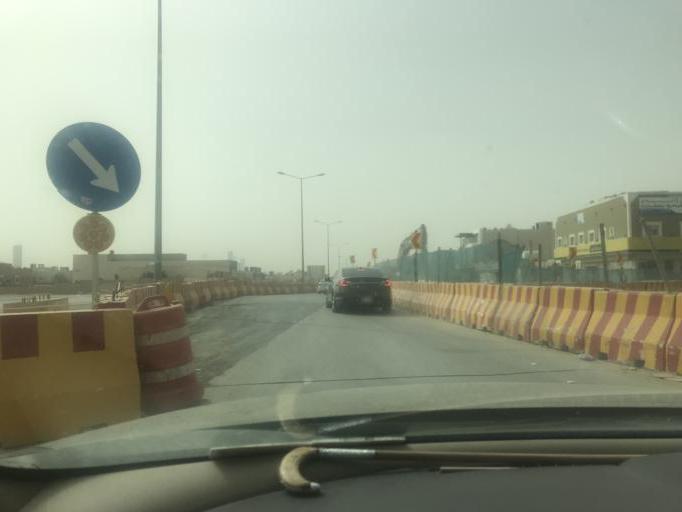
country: SA
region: Ar Riyad
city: Riyadh
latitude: 24.8119
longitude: 46.5997
